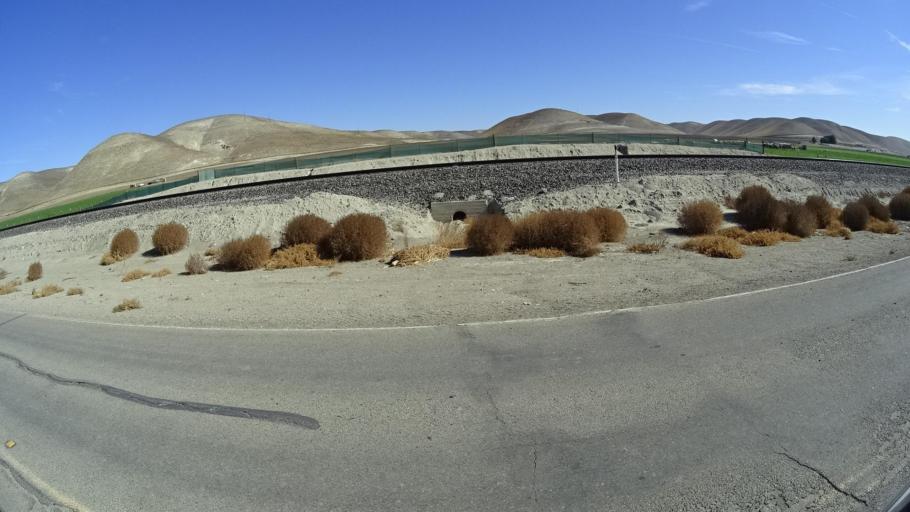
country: US
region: California
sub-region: Monterey County
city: King City
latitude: 36.0961
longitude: -120.9665
